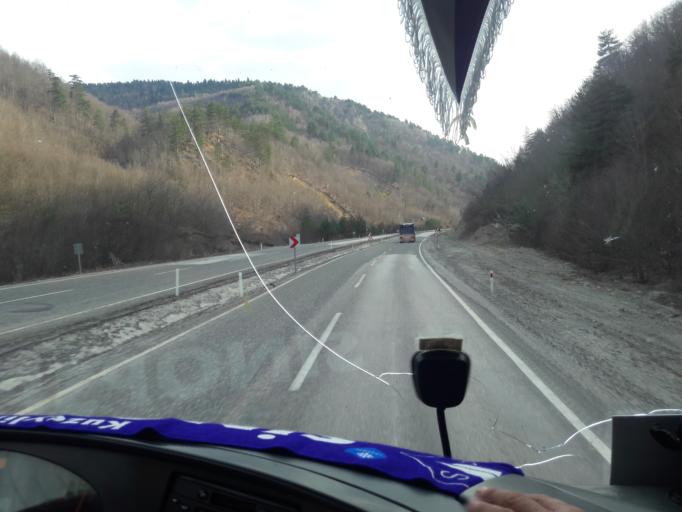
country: TR
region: Kastamonu
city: Kuzyaka
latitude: 41.1370
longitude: 33.7772
